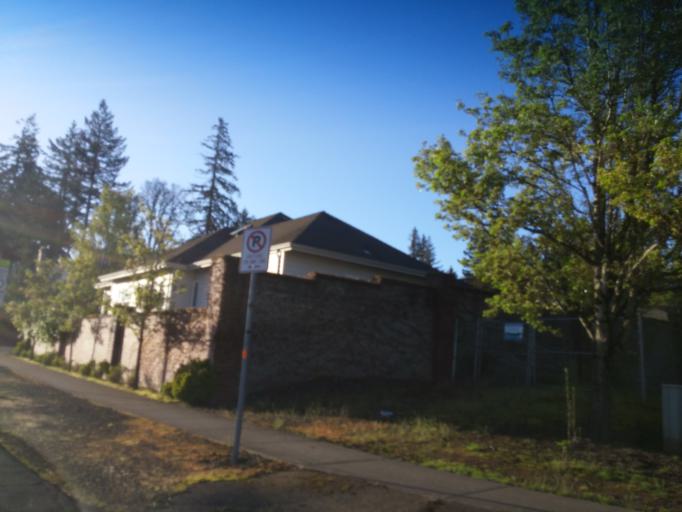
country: US
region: Oregon
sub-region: Washington County
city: Cedar Hills
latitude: 45.5064
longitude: -122.7965
